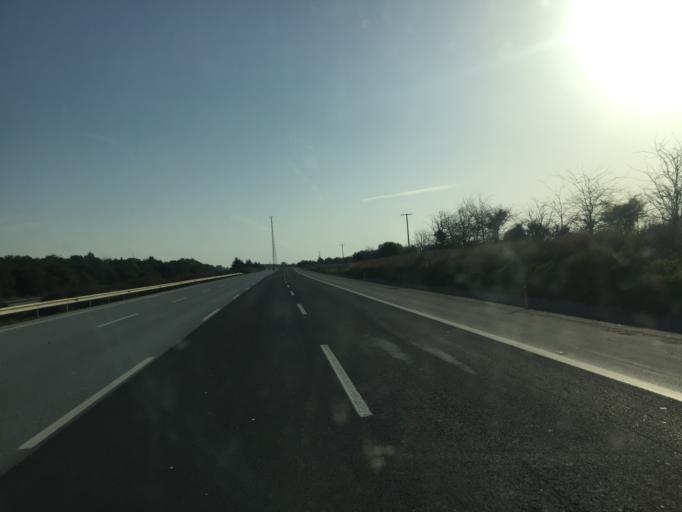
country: TR
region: Mersin
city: Yenice
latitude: 37.0231
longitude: 35.0753
